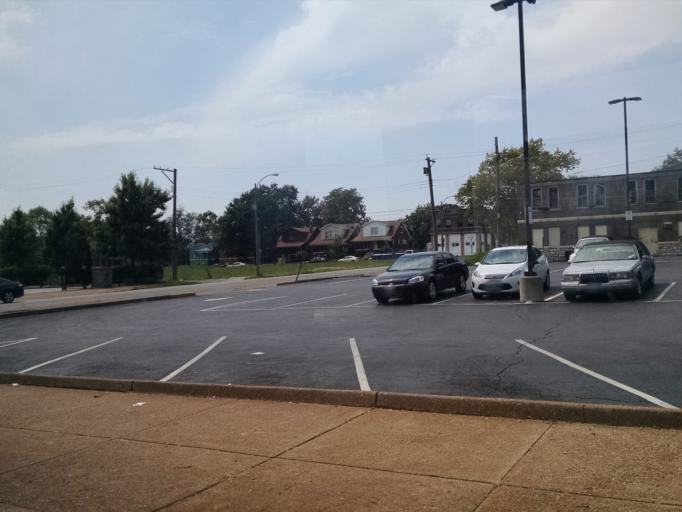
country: US
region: Illinois
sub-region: Madison County
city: Venice
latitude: 38.6685
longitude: -90.2116
